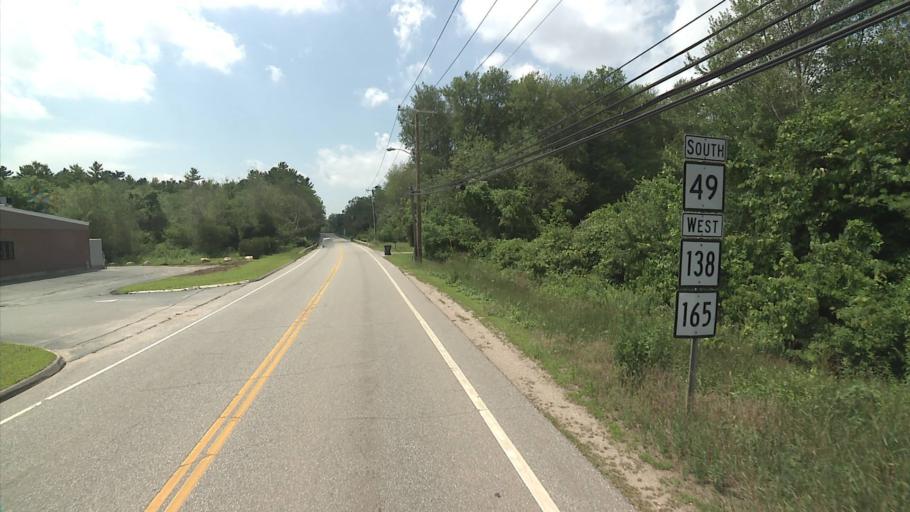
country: US
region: Connecticut
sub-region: Windham County
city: Plainfield
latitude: 41.5760
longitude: -71.8569
